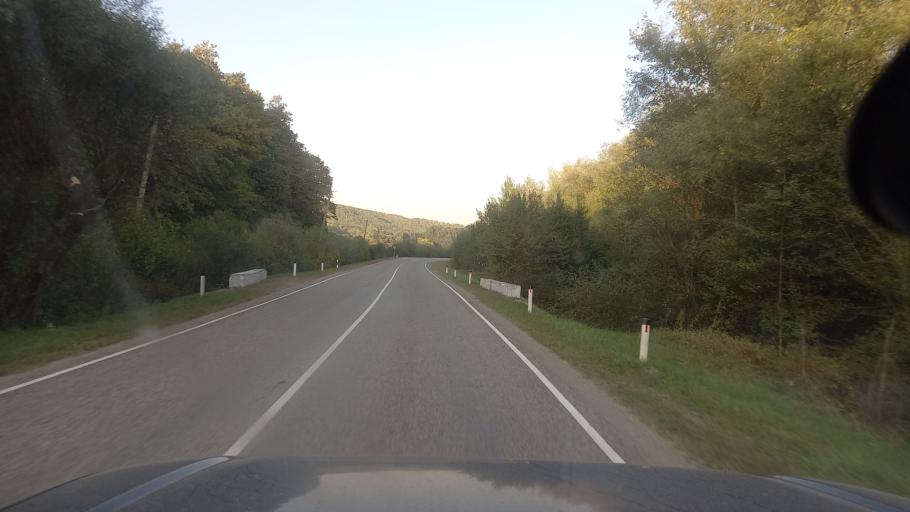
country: RU
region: Krasnodarskiy
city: Smolenskaya
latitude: 44.7364
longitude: 38.7260
